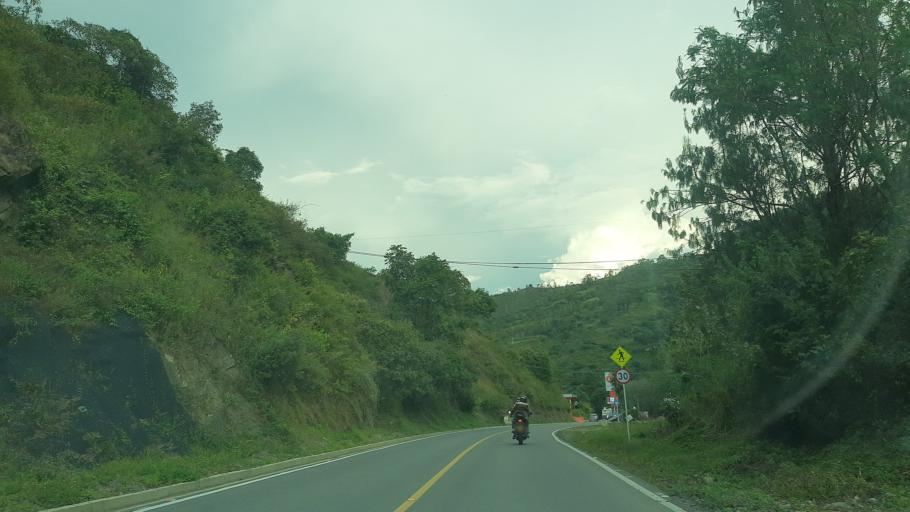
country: CO
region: Boyaca
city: Somondoco
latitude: 5.0084
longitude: -73.4043
